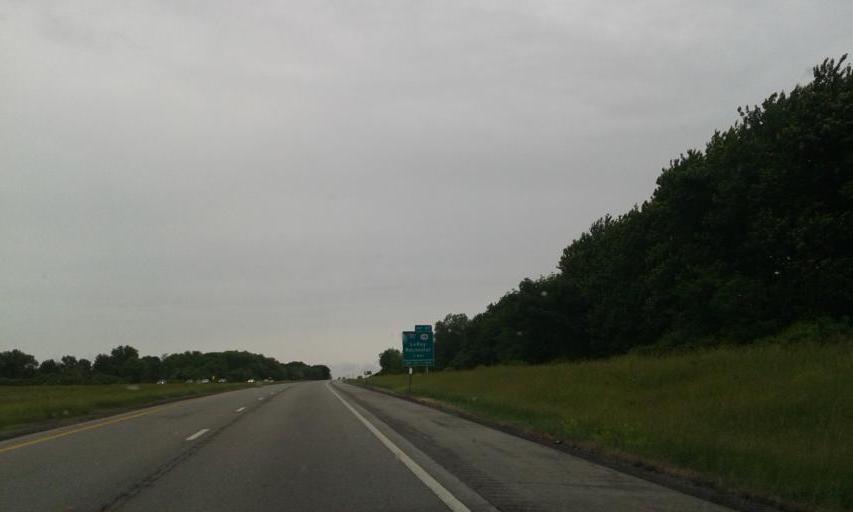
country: US
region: New York
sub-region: Genesee County
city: Bergen
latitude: 43.0291
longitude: -77.9328
